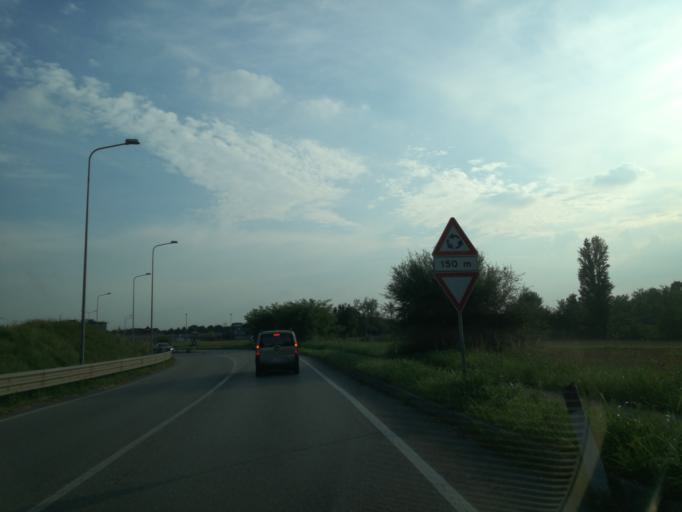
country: IT
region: Lombardy
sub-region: Citta metropolitana di Milano
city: Carugate
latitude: 45.5554
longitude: 9.3331
